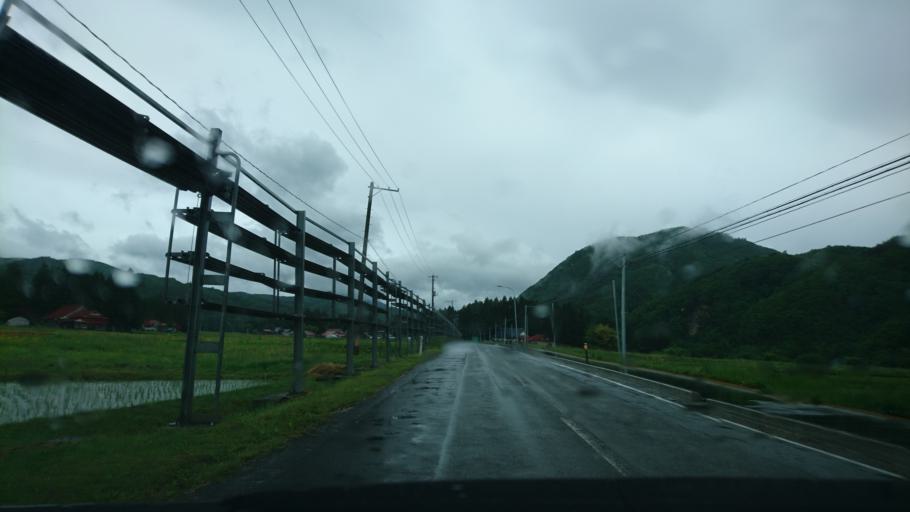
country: JP
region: Iwate
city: Ichinoseki
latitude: 38.9799
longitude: 140.9196
